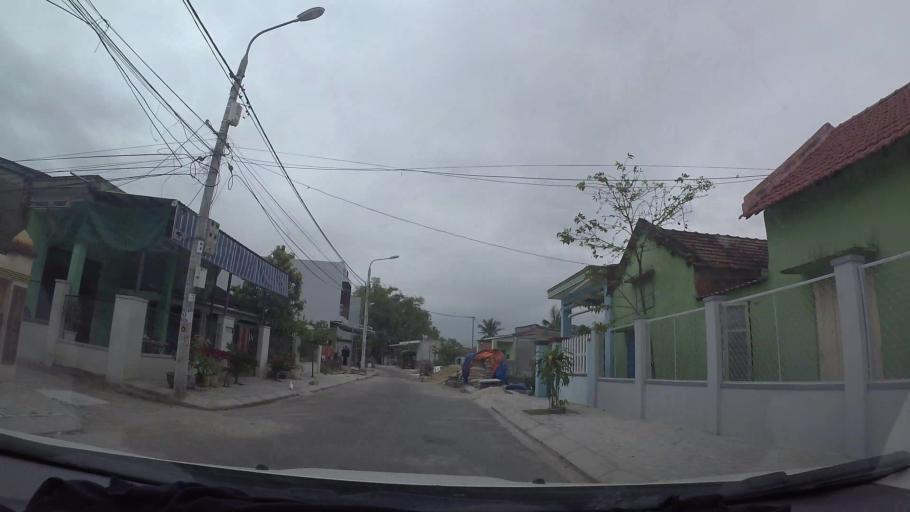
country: VN
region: Da Nang
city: Lien Chieu
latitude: 16.1065
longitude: 108.1291
